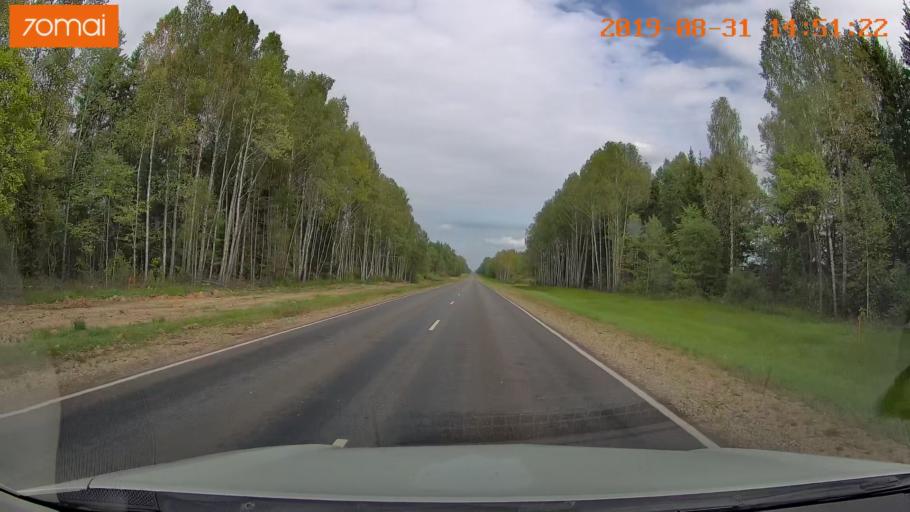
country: RU
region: Kaluga
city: Spas-Demensk
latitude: 54.2681
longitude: 33.8127
